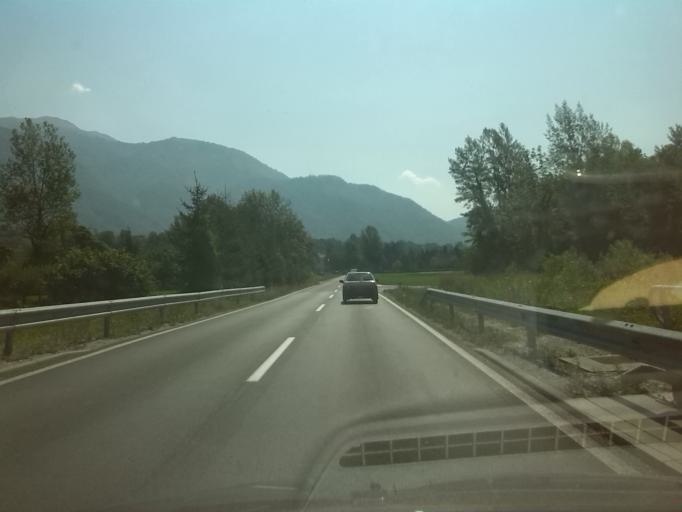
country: SI
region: Tolmin
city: Tolmin
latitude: 46.1831
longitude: 13.7203
